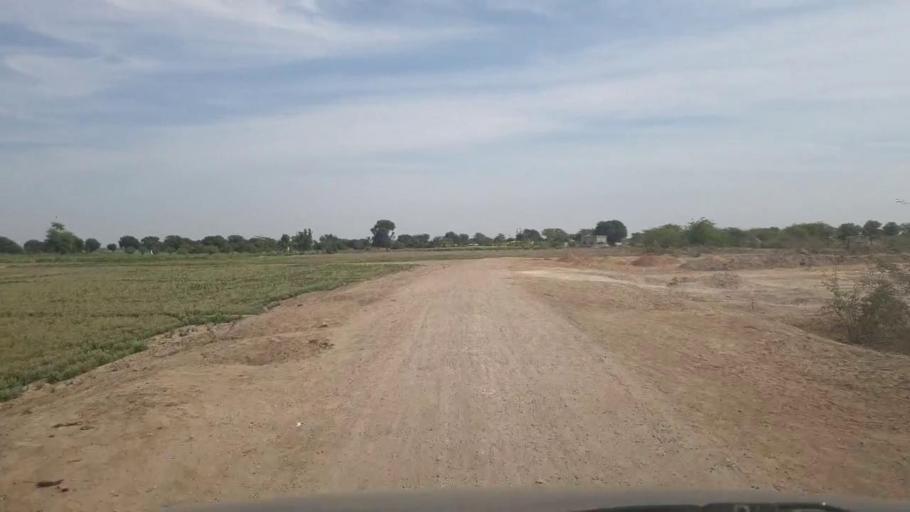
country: PK
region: Sindh
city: Kunri
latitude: 25.2383
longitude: 69.6442
